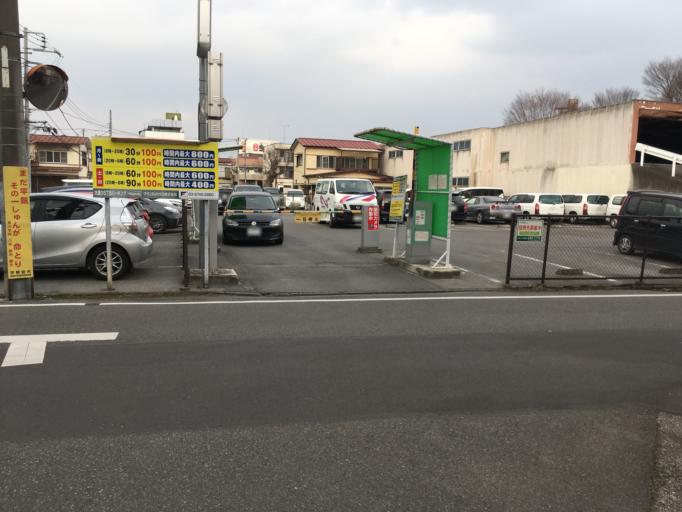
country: JP
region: Tochigi
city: Utsunomiya-shi
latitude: 36.5618
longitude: 139.8923
